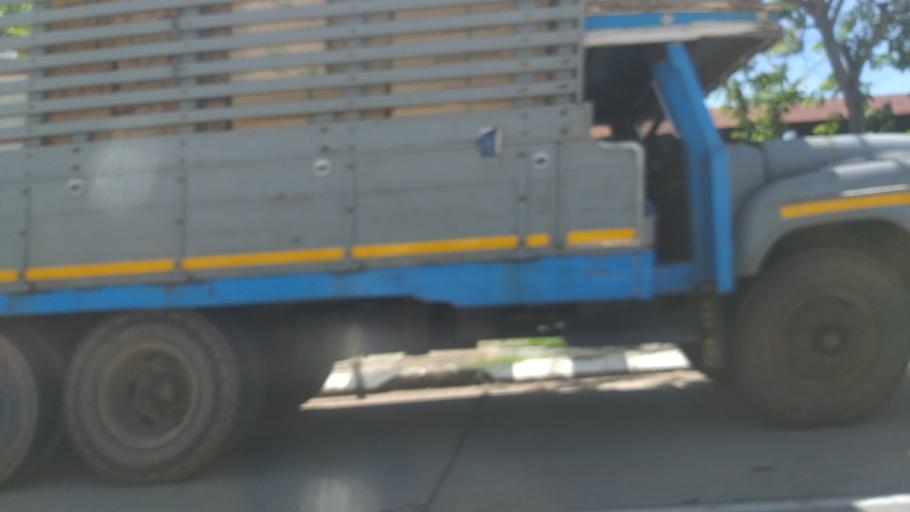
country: TH
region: Khon Kaen
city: Khon Kaen
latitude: 16.4332
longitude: 102.8194
